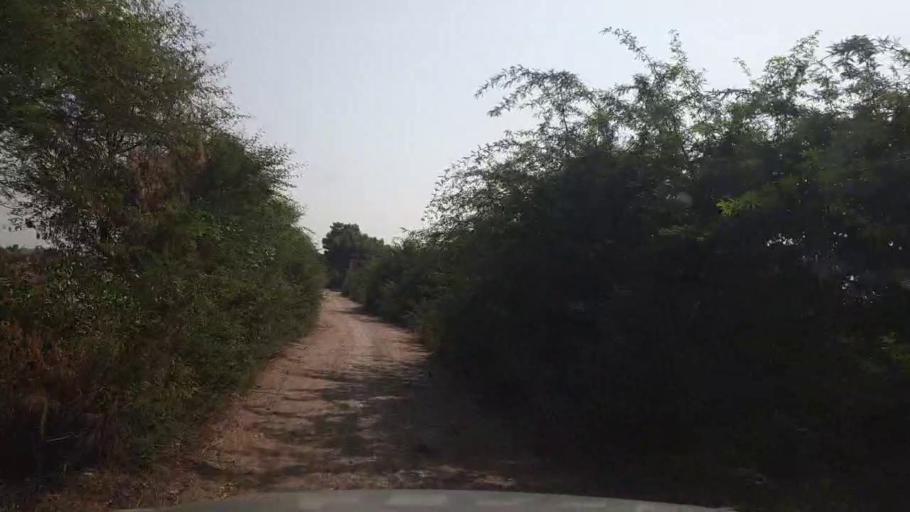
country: PK
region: Sindh
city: Bhit Shah
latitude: 25.7369
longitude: 68.4970
